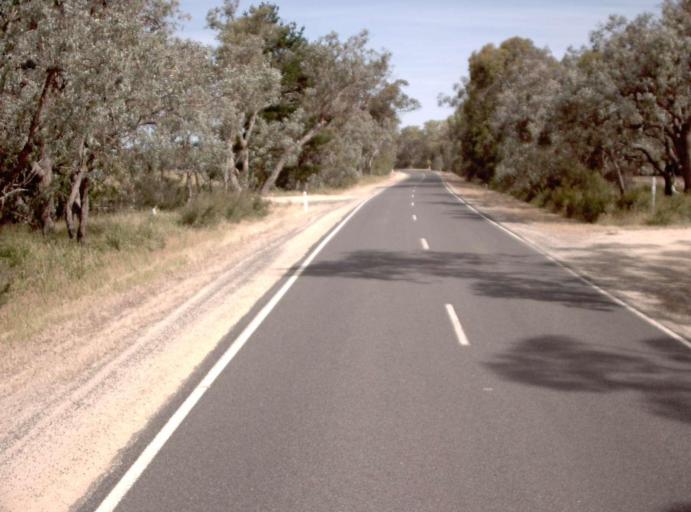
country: AU
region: Victoria
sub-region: Wellington
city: Sale
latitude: -38.2479
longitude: 147.1321
